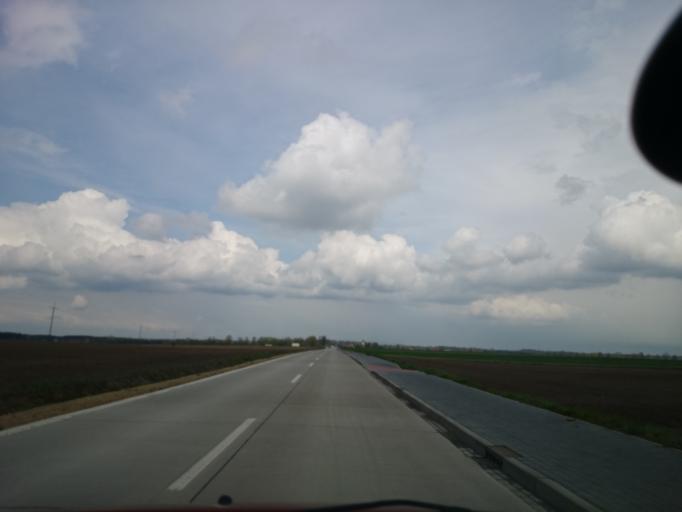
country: PL
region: Opole Voivodeship
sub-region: Powiat strzelecki
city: Izbicko
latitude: 50.5615
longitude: 18.1508
